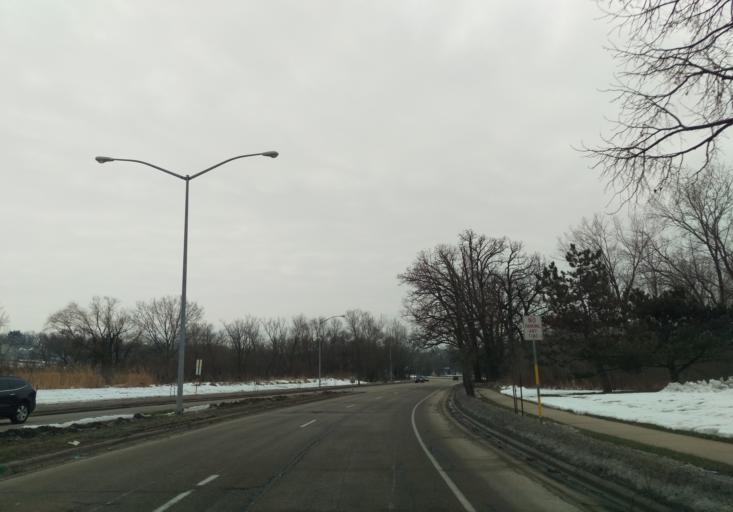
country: US
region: Wisconsin
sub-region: Dane County
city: Monona
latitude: 43.1251
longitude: -89.3002
